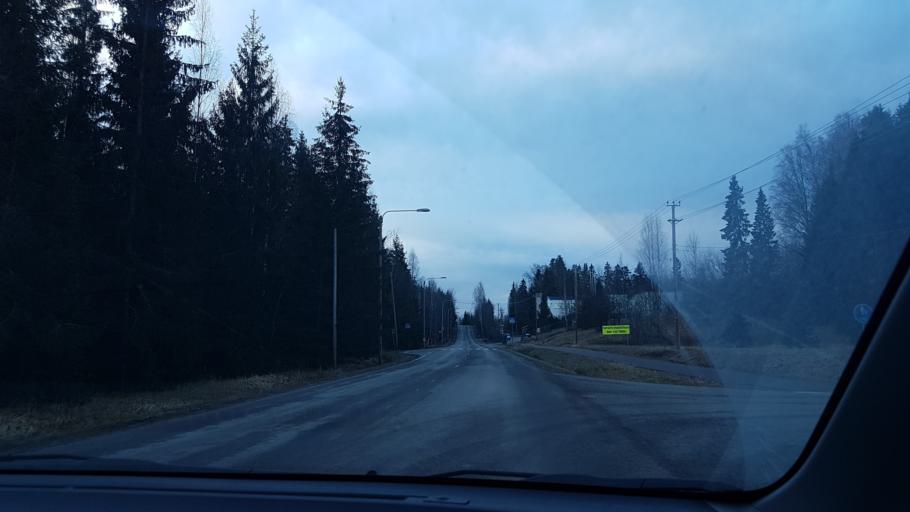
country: FI
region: Uusimaa
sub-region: Helsinki
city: Nurmijaervi
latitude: 60.3603
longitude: 24.7446
